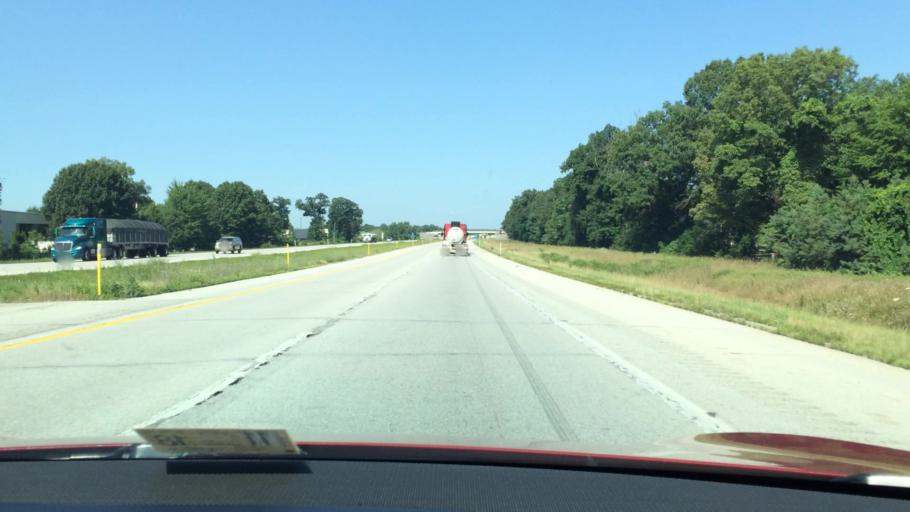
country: US
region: Indiana
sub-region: Elkhart County
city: Simonton Lake
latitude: 41.7293
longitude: -85.9040
